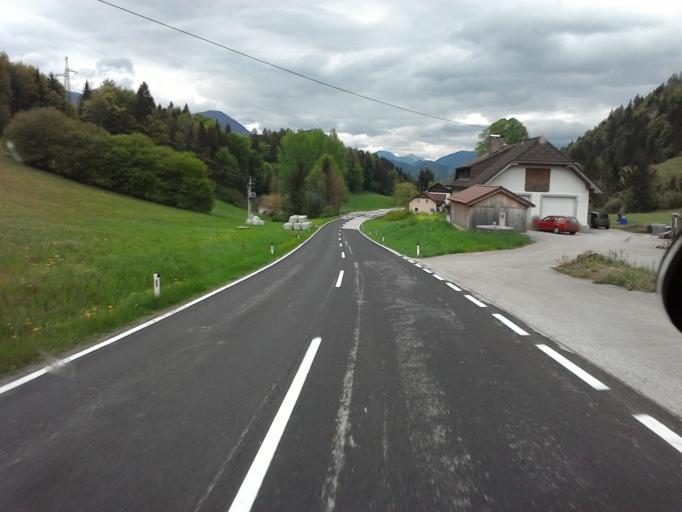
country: AT
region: Upper Austria
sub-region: Politischer Bezirk Kirchdorf an der Krems
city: Rossleithen
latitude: 47.7481
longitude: 14.2416
